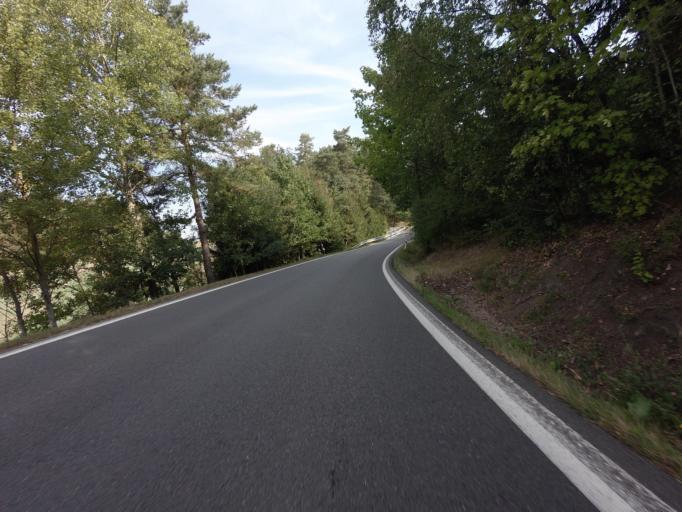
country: CZ
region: Central Bohemia
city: Petrovice
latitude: 49.5319
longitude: 14.3527
